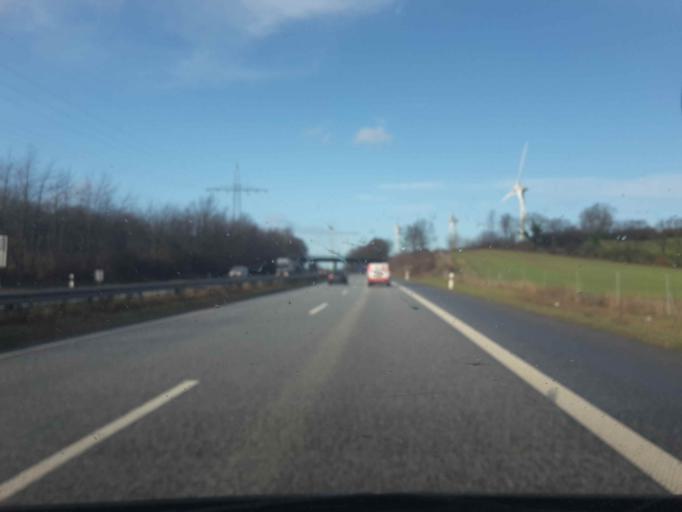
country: DE
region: Schleswig-Holstein
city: Kabelhorst
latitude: 54.2189
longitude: 10.9023
